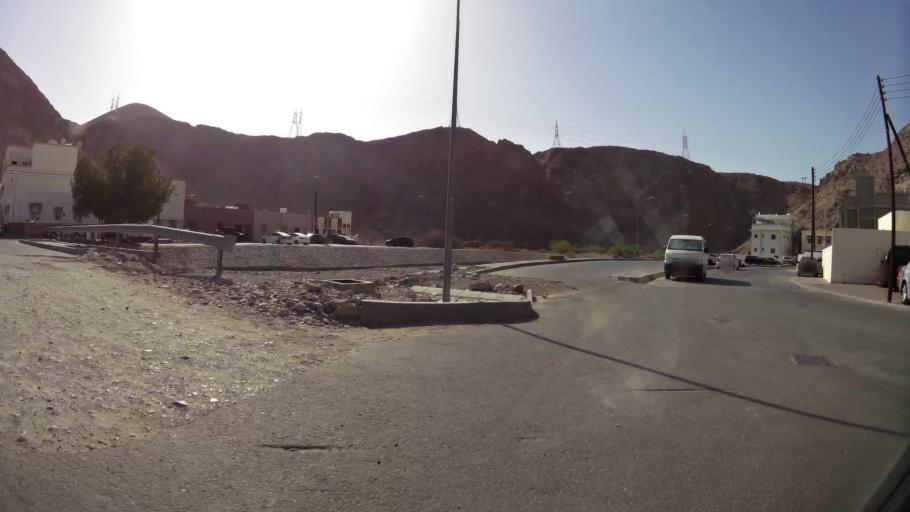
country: OM
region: Muhafazat Masqat
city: Muscat
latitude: 23.5854
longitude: 58.5154
